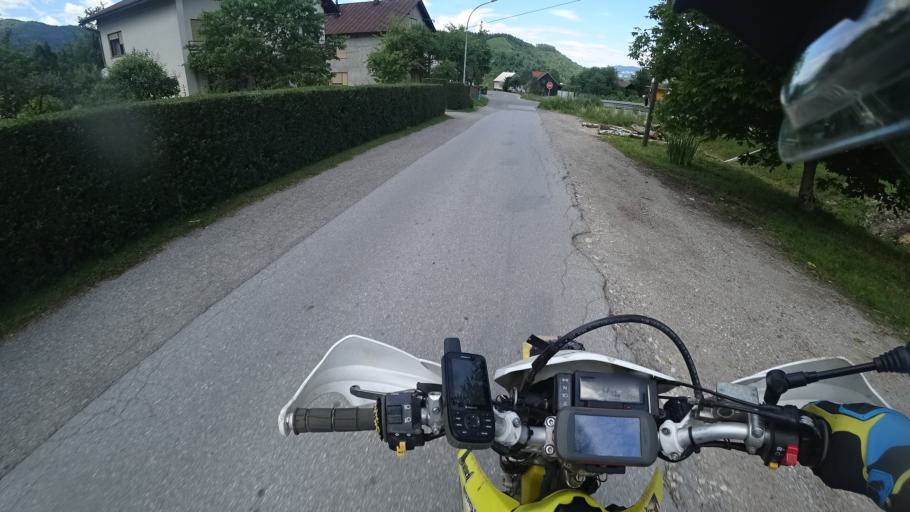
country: SI
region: Osilnica
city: Osilnica
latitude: 45.5104
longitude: 14.6355
